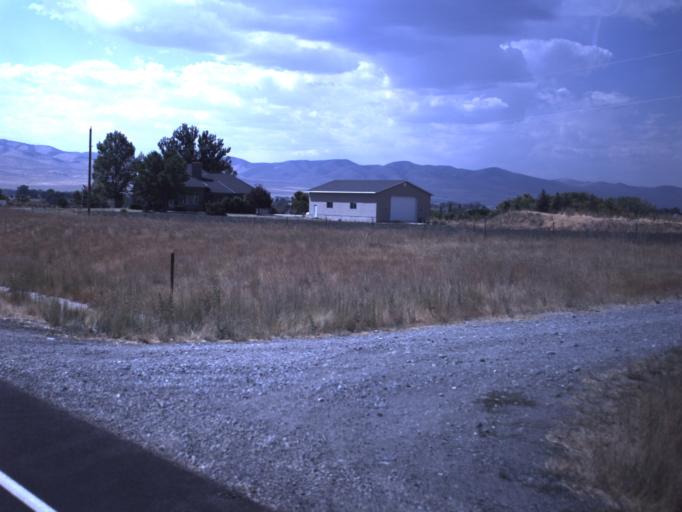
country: US
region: Utah
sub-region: Box Elder County
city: Garland
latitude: 41.7838
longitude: -112.1023
